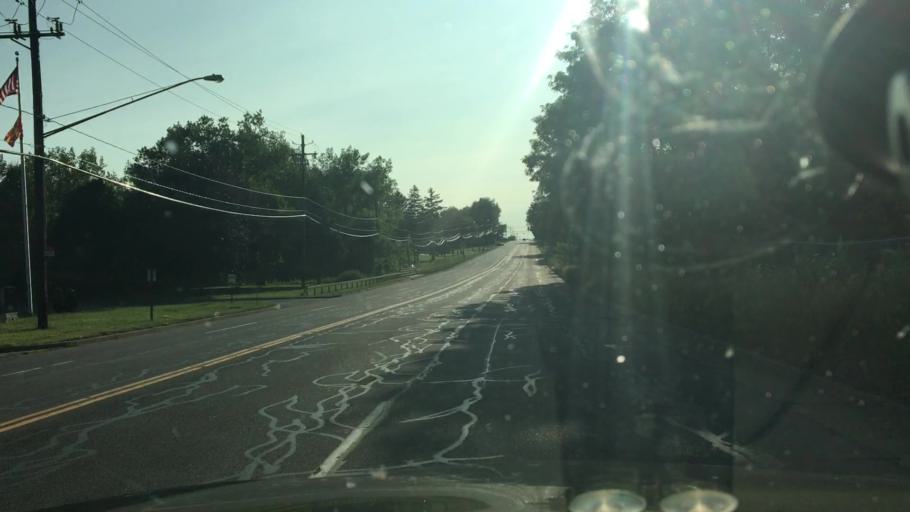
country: US
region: New York
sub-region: Erie County
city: Blasdell
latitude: 42.7969
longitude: -78.8027
